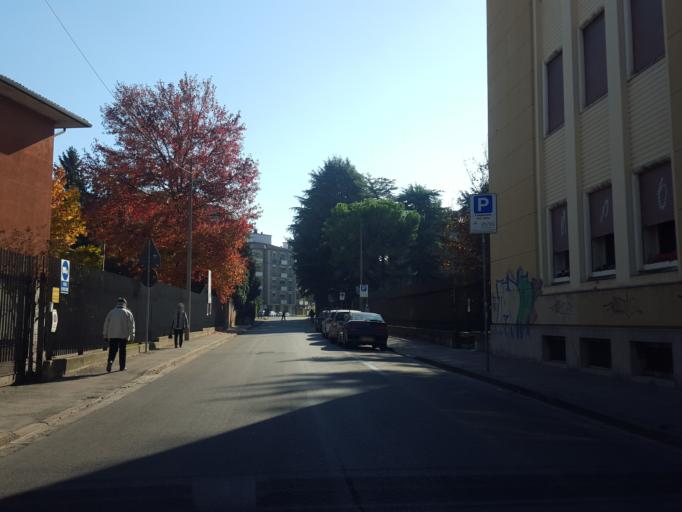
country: IT
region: Veneto
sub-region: Provincia di Vicenza
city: Vicenza
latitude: 45.5483
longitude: 11.5526
